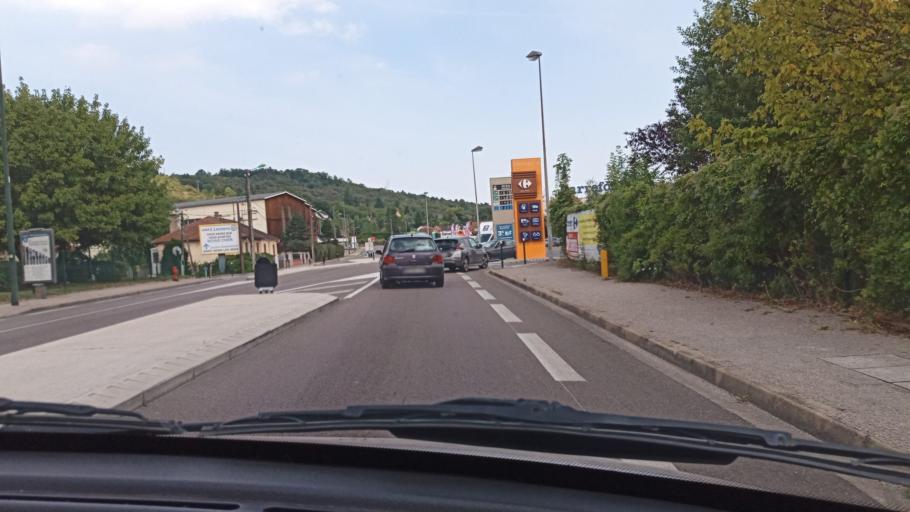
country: FR
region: Bourgogne
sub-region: Departement de l'Yonne
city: Sens
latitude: 48.1974
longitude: 3.2654
